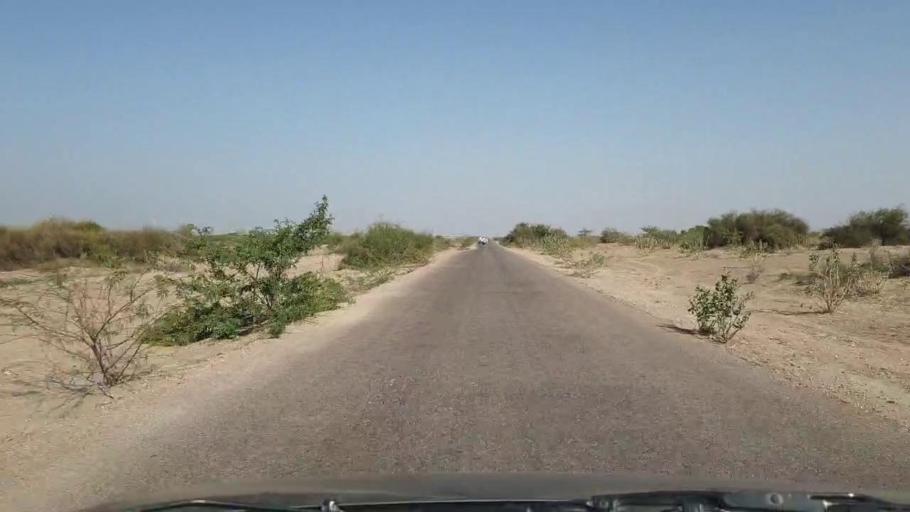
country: PK
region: Sindh
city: Chor
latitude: 25.5126
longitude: 69.8187
